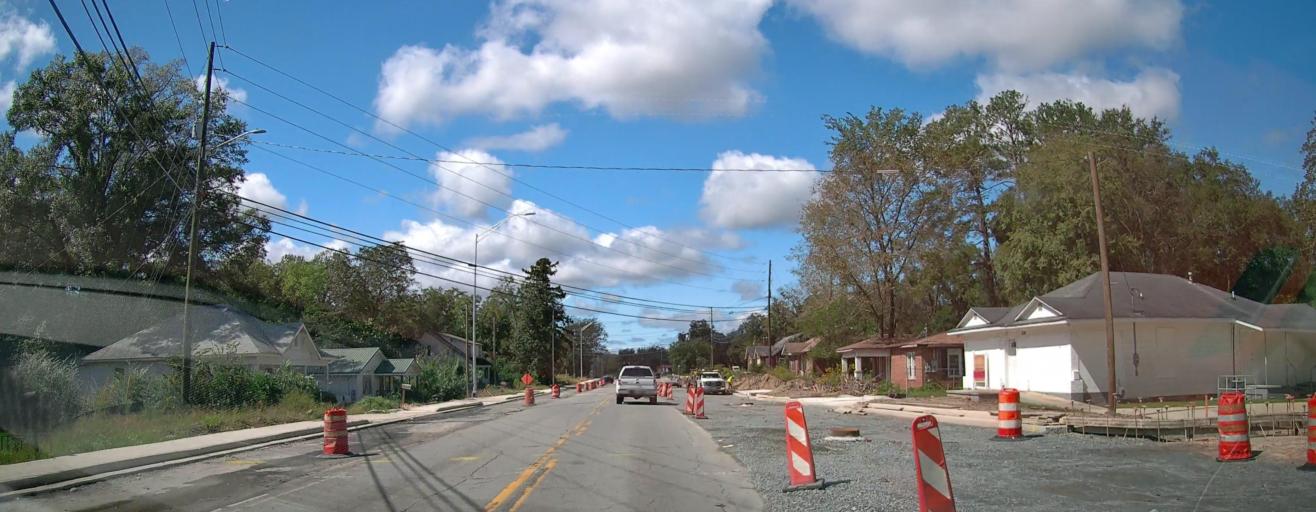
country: US
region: Georgia
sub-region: Bibb County
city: Macon
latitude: 32.8513
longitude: -83.5844
